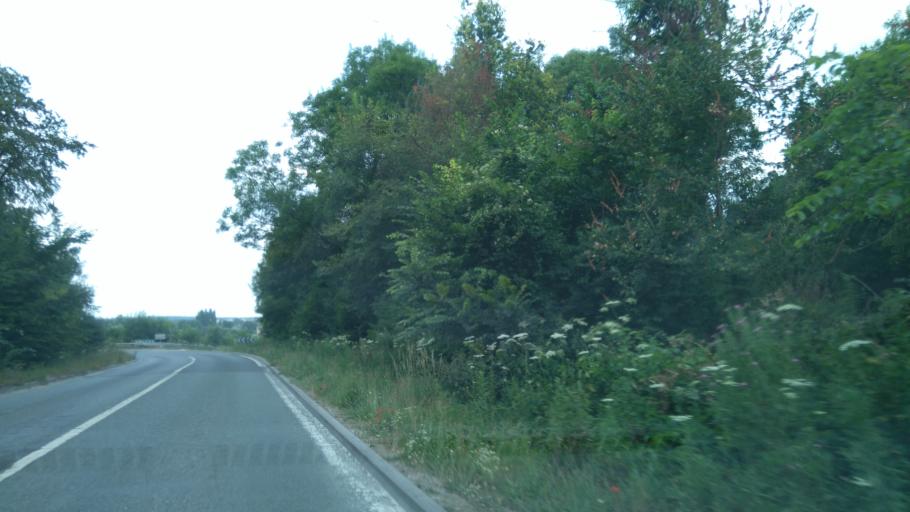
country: FR
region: Picardie
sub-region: Departement de l'Oise
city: Saint-Maximin
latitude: 49.2122
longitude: 2.4330
